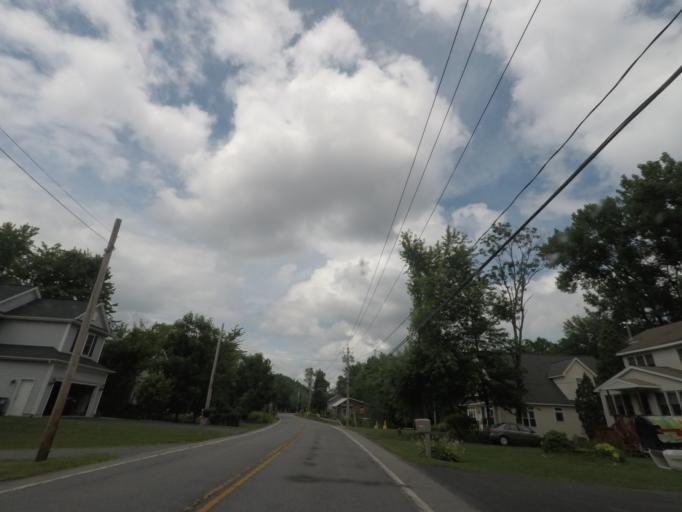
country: US
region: New York
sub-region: Saratoga County
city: Saratoga Springs
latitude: 42.9983
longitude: -73.7353
